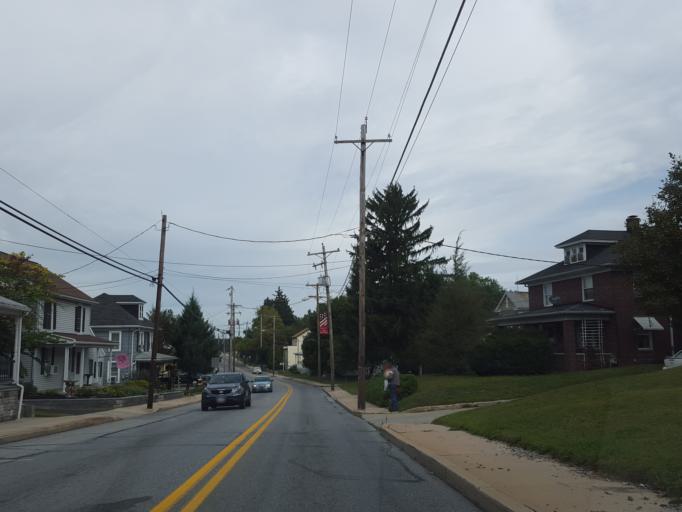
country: US
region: Pennsylvania
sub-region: York County
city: West York
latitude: 39.9026
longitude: -76.7893
